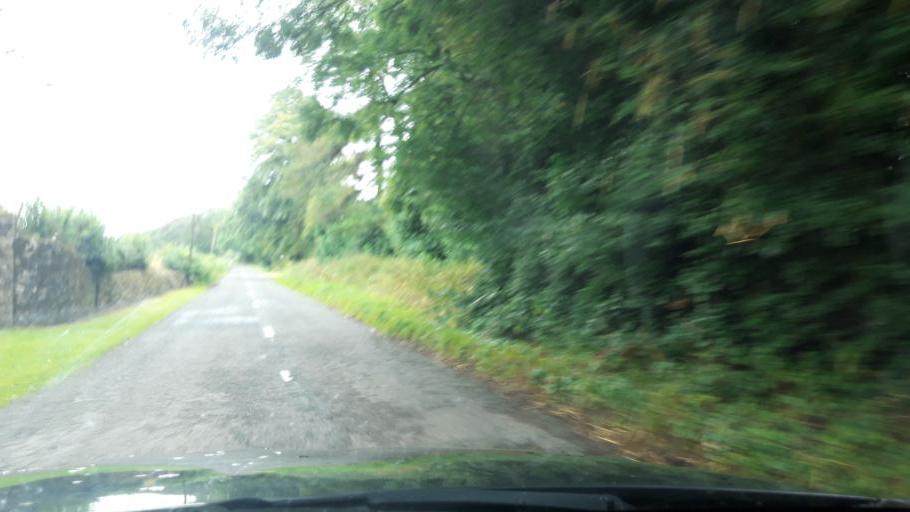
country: IE
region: Munster
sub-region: County Cork
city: Castlemartyr
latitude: 52.1357
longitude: -8.0381
